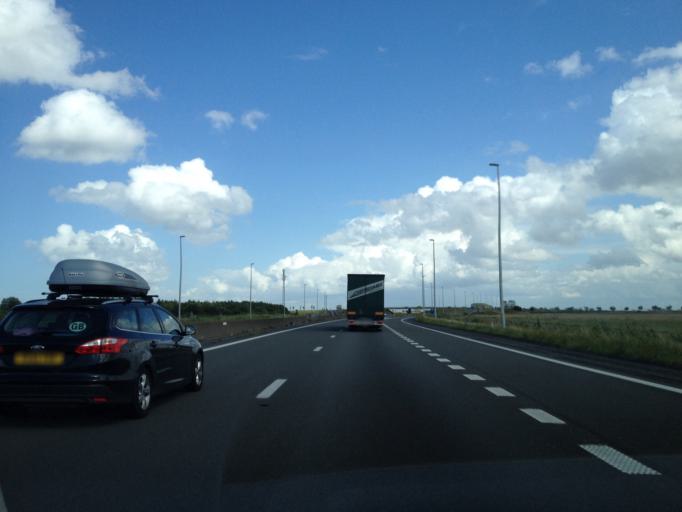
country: BE
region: Flanders
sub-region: Provincie West-Vlaanderen
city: De Panne
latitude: 51.0670
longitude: 2.5953
